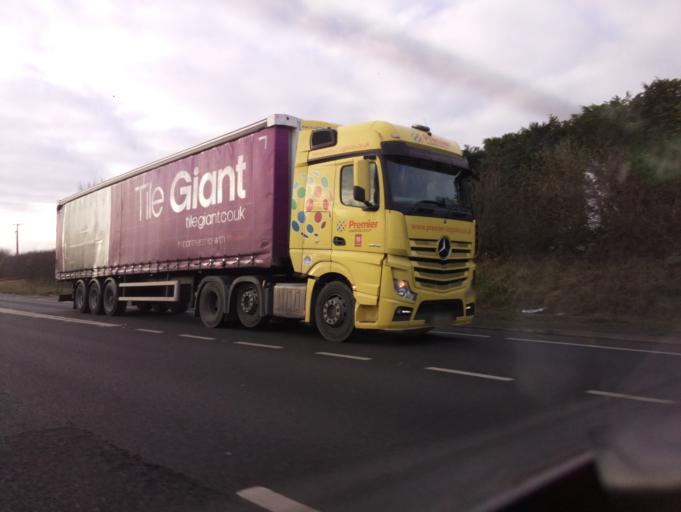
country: GB
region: England
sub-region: Staffordshire
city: Shenstone
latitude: 52.6436
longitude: -1.8055
